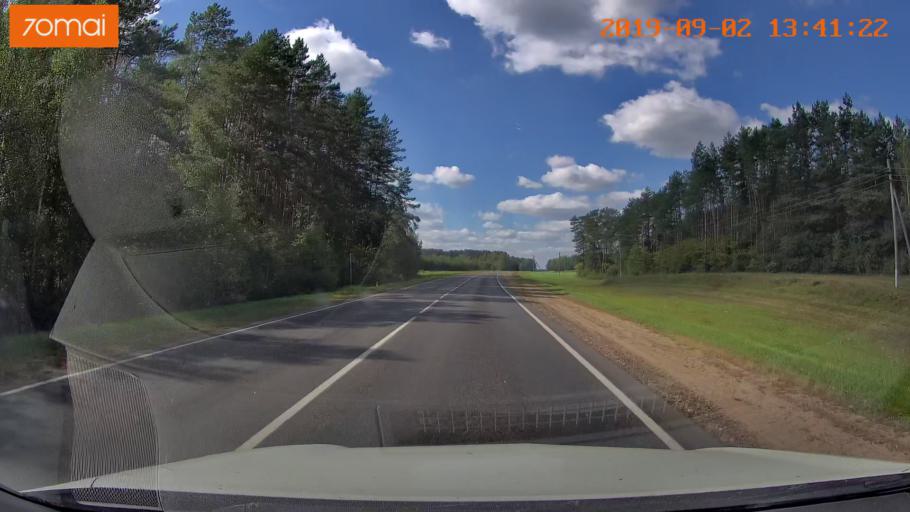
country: BY
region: Mogilev
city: Cherykaw
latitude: 53.5941
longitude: 31.4299
